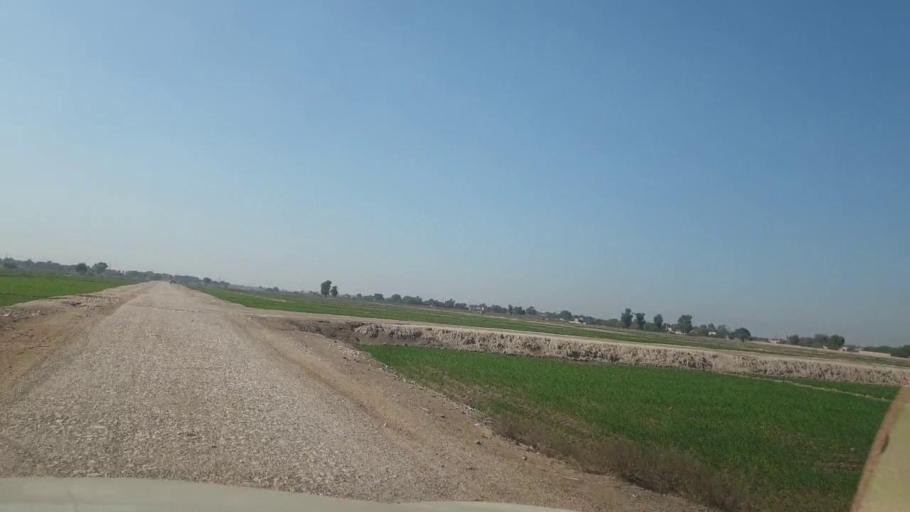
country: PK
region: Sindh
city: Bhan
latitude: 26.5643
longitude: 67.6923
